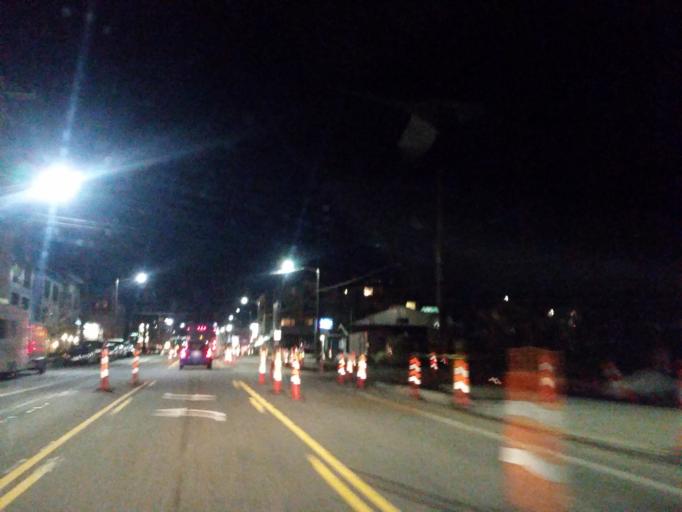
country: US
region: Washington
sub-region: King County
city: Shoreline
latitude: 47.7027
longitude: -122.3554
